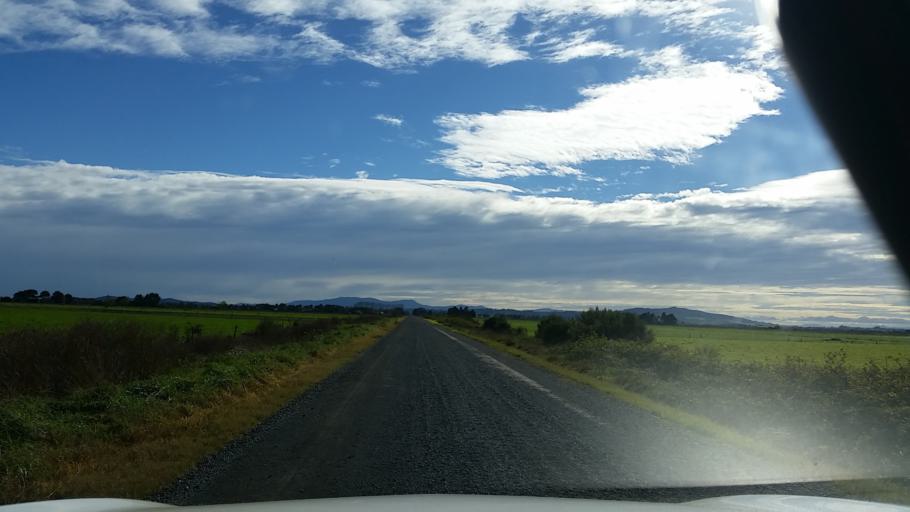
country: NZ
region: Waikato
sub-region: Hamilton City
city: Hamilton
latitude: -37.6816
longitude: 175.4436
